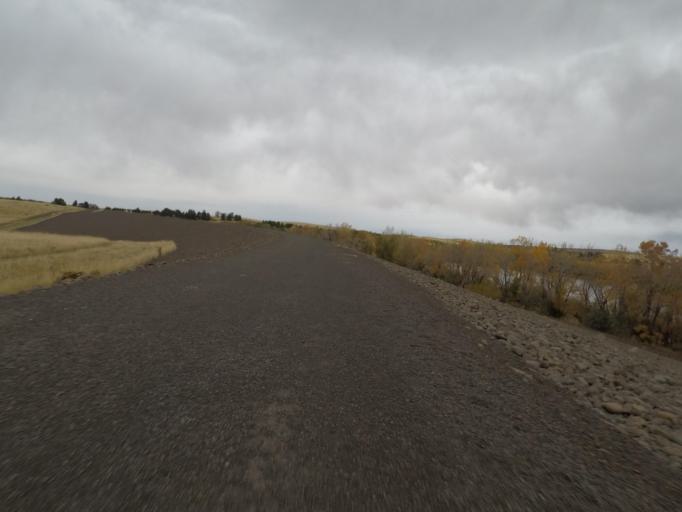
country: US
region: Washington
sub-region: Walla Walla County
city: Walla Walla East
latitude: 46.0618
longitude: -118.2607
